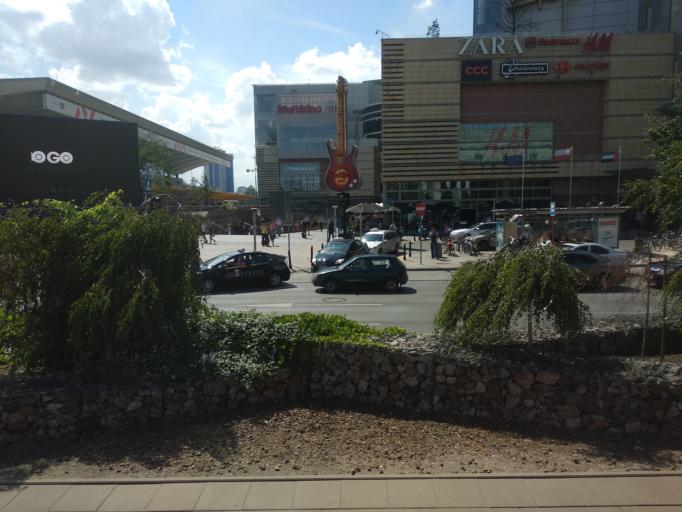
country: PL
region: Masovian Voivodeship
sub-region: Warszawa
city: Warsaw
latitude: 52.2300
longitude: 21.0047
